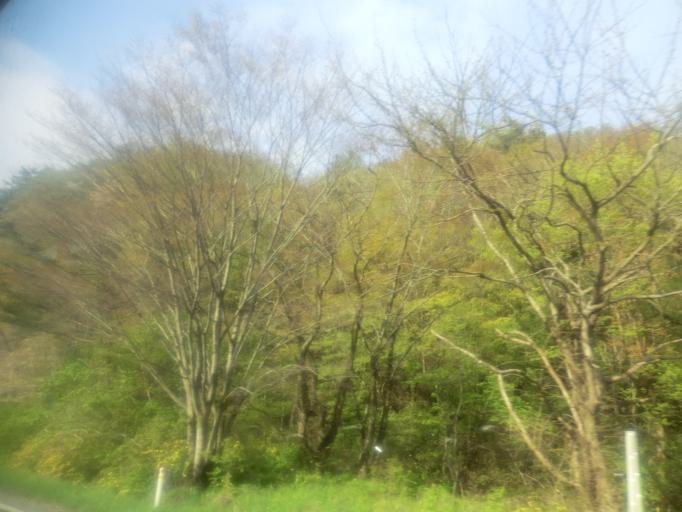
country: JP
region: Iwate
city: Miyako
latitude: 39.5570
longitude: 141.9403
